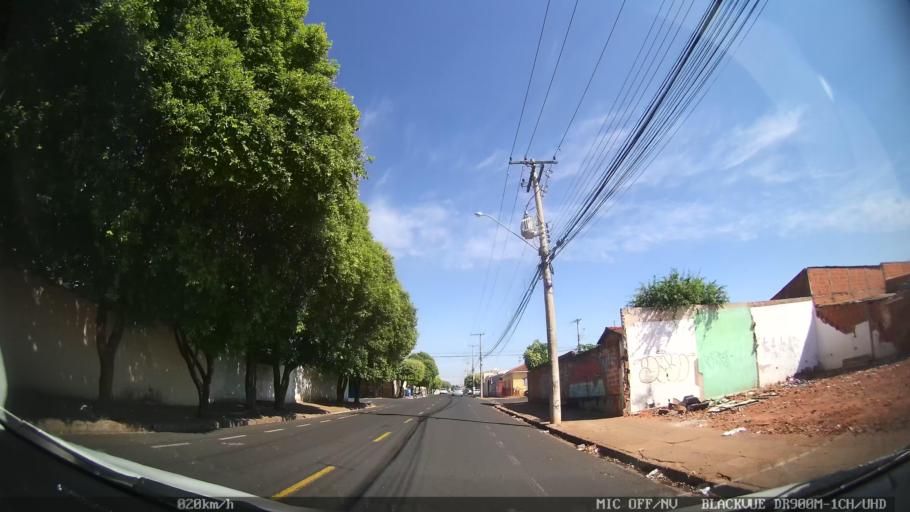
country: BR
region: Sao Paulo
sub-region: Sao Jose Do Rio Preto
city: Sao Jose do Rio Preto
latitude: -20.7783
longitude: -49.4060
